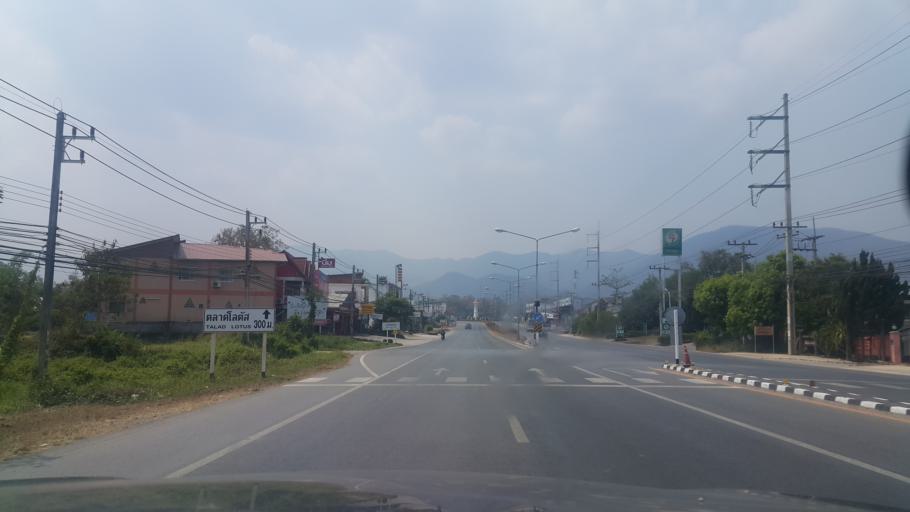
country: TH
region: Lamphun
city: Ban Hong
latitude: 18.3033
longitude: 98.8188
